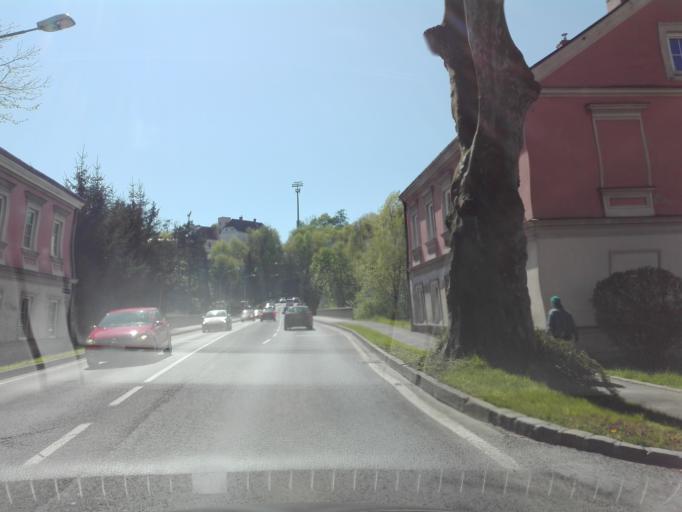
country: AT
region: Upper Austria
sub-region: Steyr Stadt
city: Steyr
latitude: 48.0405
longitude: 14.4088
